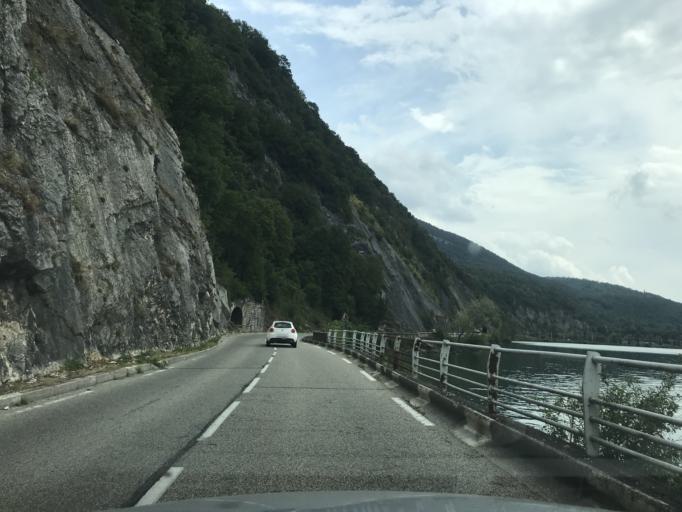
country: FR
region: Rhone-Alpes
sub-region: Departement de la Savoie
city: Brison-Saint-Innocent
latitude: 45.7436
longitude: 5.8877
